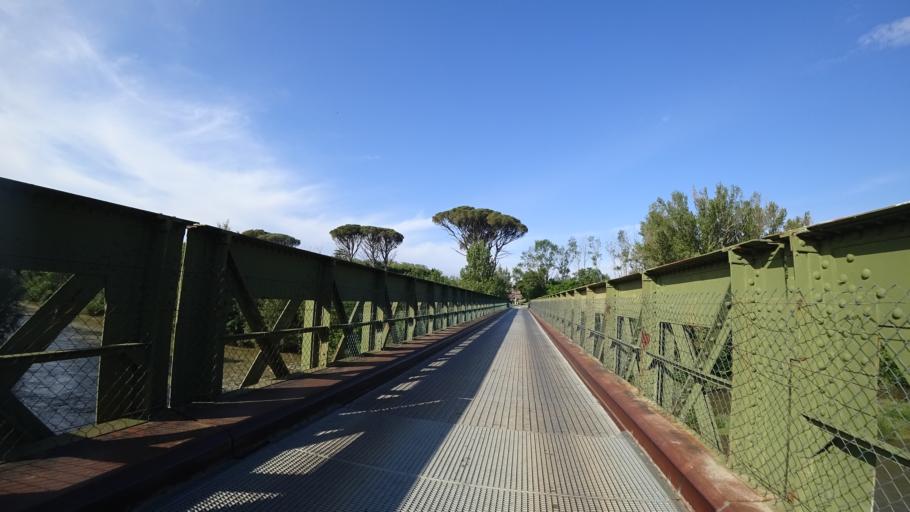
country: FR
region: Languedoc-Roussillon
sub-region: Departement de l'Aude
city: Lezignan-Corbieres
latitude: 43.2389
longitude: 2.7631
